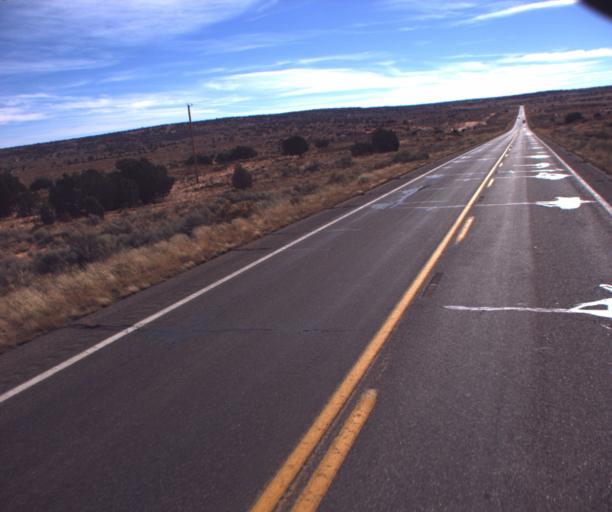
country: US
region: Arizona
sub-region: Coconino County
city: Kaibito
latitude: 36.5933
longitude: -111.1609
